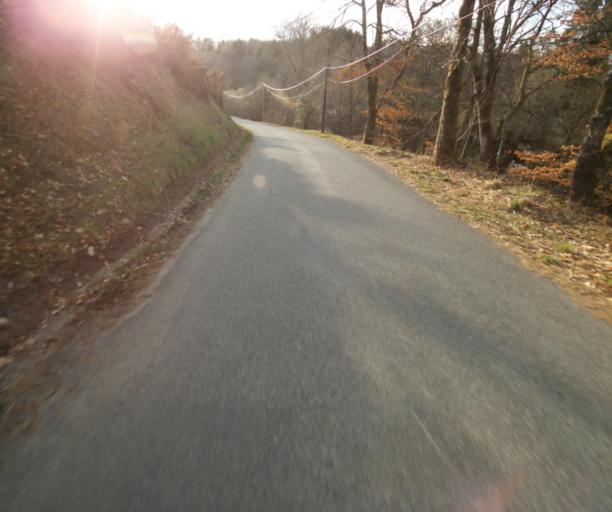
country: FR
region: Limousin
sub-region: Departement de la Correze
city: Correze
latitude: 45.3836
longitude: 1.8548
